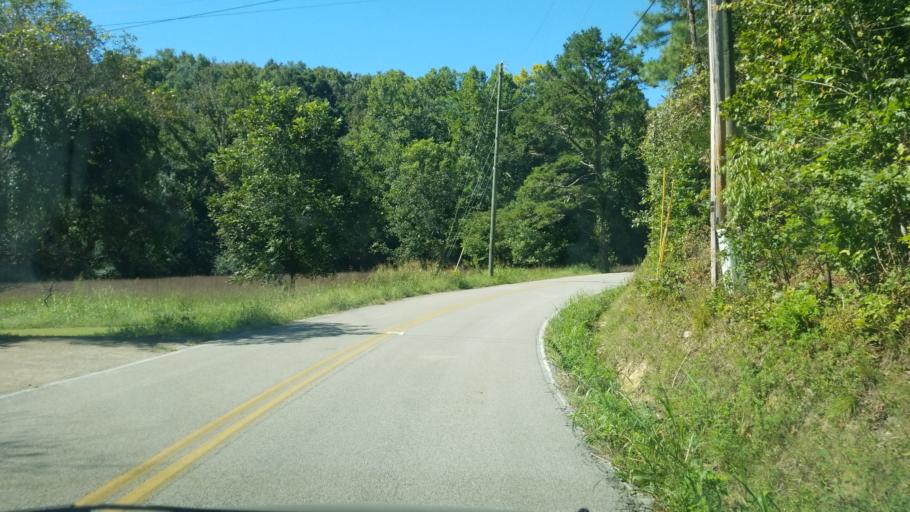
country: US
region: Tennessee
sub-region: Hamilton County
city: Harrison
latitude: 35.0981
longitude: -85.0852
